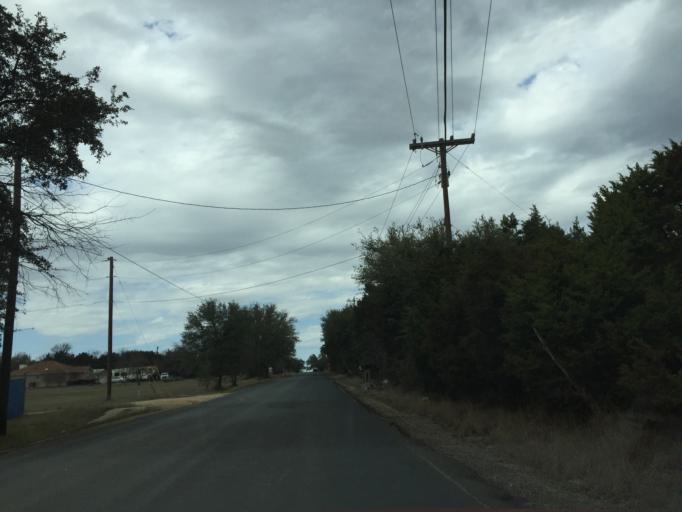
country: US
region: Texas
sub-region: Burnet County
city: Bertram
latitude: 30.7229
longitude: -97.9314
